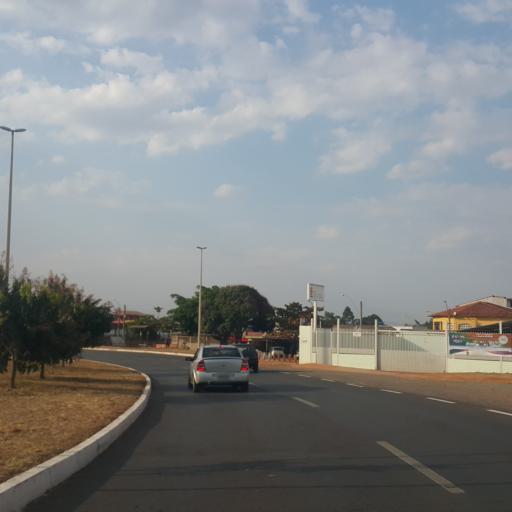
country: BR
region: Federal District
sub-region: Brasilia
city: Brasilia
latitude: -15.8680
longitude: -48.0234
